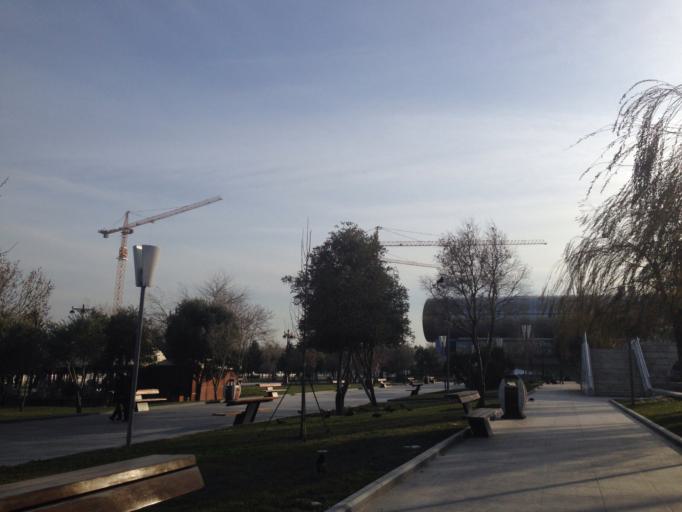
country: AZ
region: Baki
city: Badamdar
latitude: 40.3611
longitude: 49.8363
